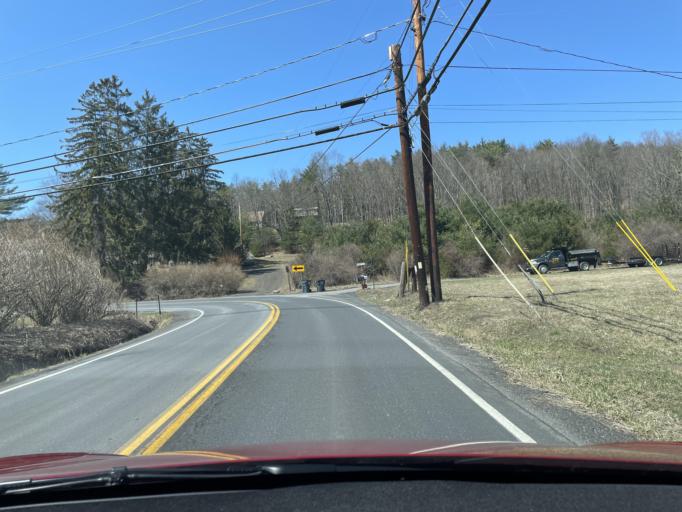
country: US
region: New York
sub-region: Ulster County
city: Woodstock
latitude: 42.0373
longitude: -74.1719
